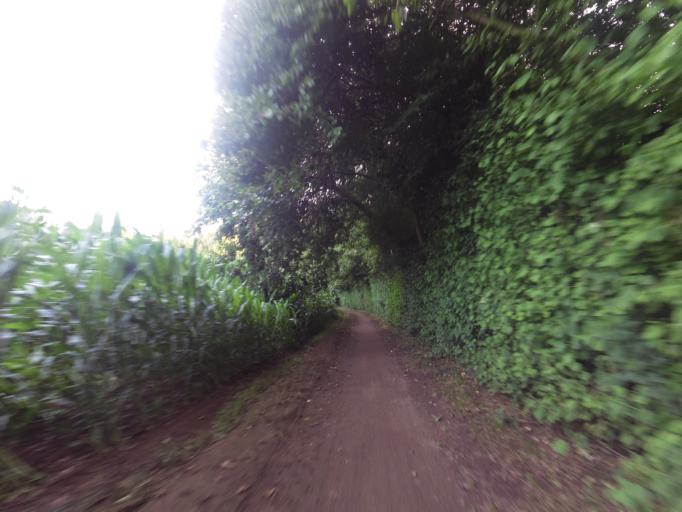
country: DE
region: North Rhine-Westphalia
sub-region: Regierungsbezirk Munster
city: Isselburg
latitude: 51.8834
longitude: 6.4761
